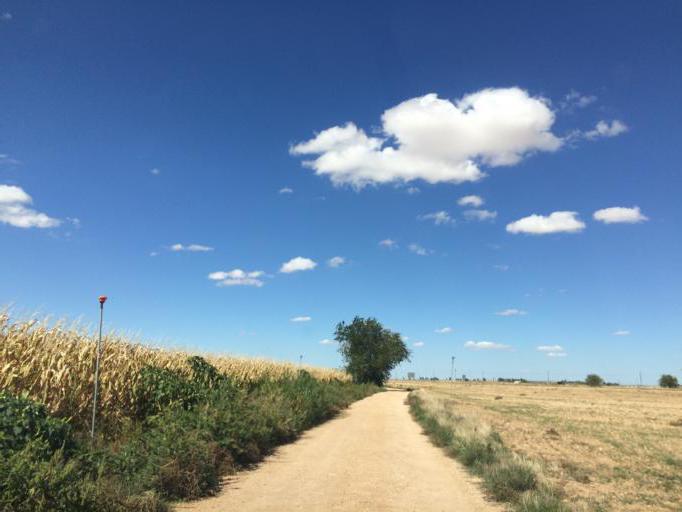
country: ES
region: Castille-La Mancha
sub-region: Provincia de Albacete
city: Albacete
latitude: 38.9409
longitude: -1.8385
